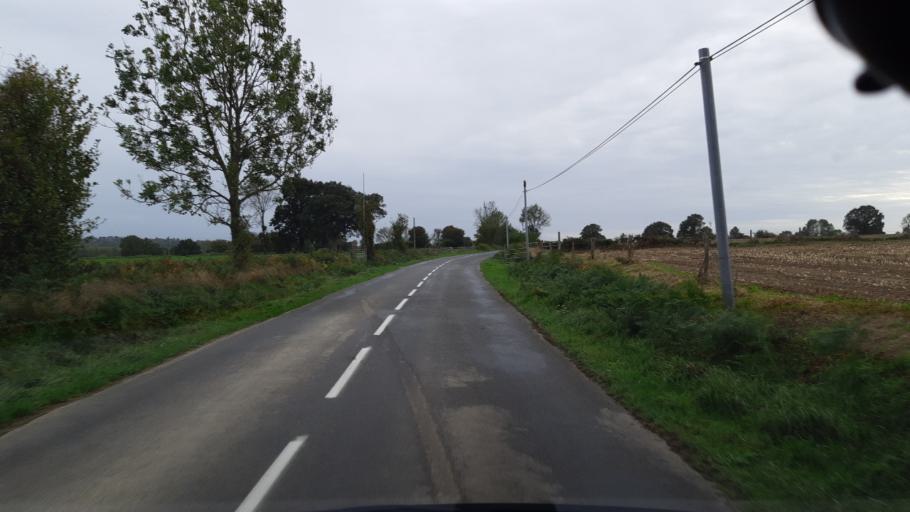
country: FR
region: Lower Normandy
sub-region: Departement de la Manche
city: Hambye
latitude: 48.9665
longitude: -1.2601
